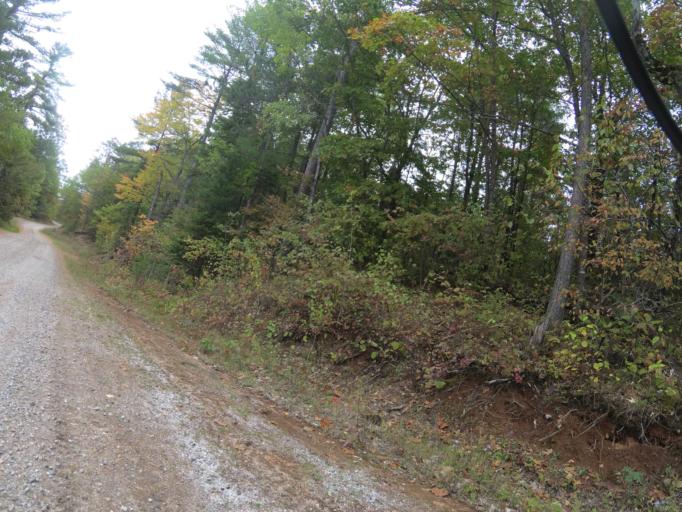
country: CA
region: Ontario
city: Renfrew
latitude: 45.2065
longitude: -77.0760
